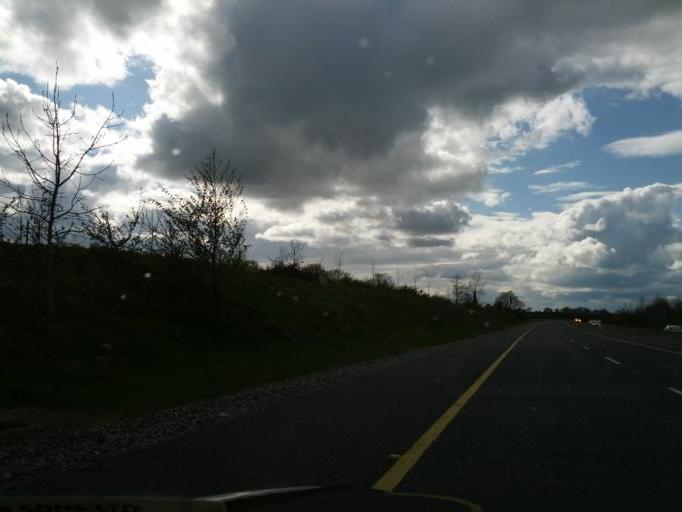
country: IE
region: Leinster
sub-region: An Iarmhi
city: Kilbeggan
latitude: 53.3602
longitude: -7.5122
